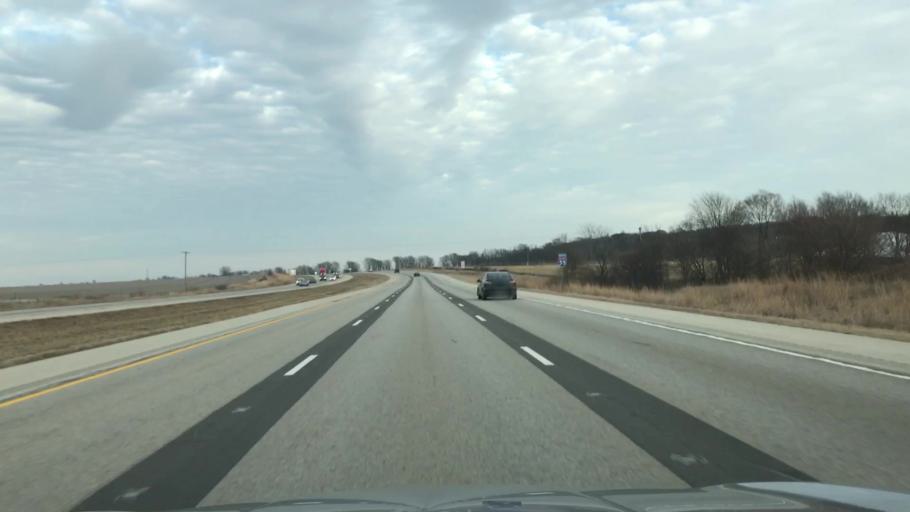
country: US
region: Illinois
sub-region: Sangamon County
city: Williamsville
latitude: 40.0251
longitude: -89.4859
